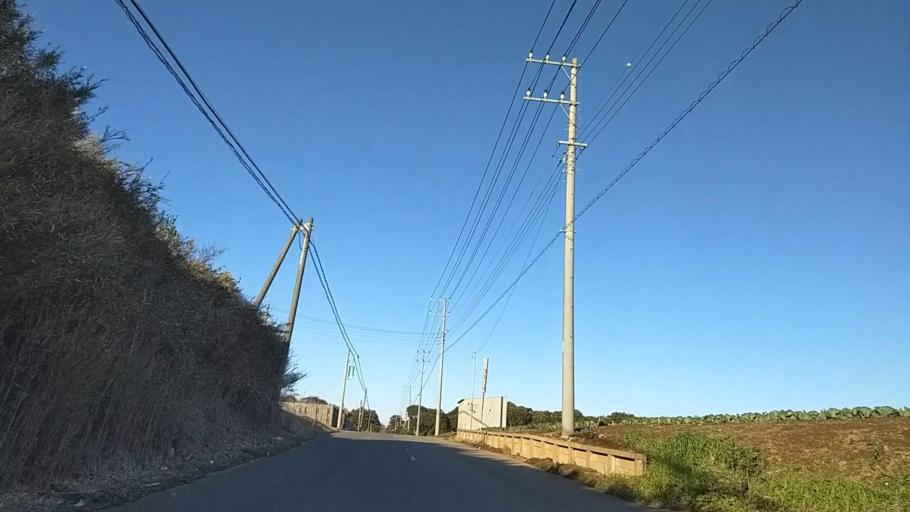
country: JP
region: Chiba
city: Asahi
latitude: 35.7269
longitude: 140.7371
